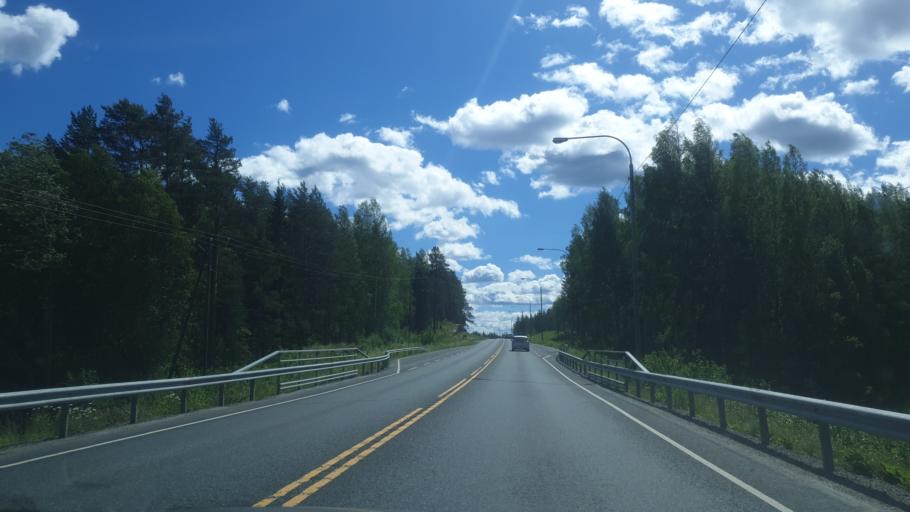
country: FI
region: Northern Savo
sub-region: Varkaus
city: Leppaevirta
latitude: 62.5308
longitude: 27.6570
